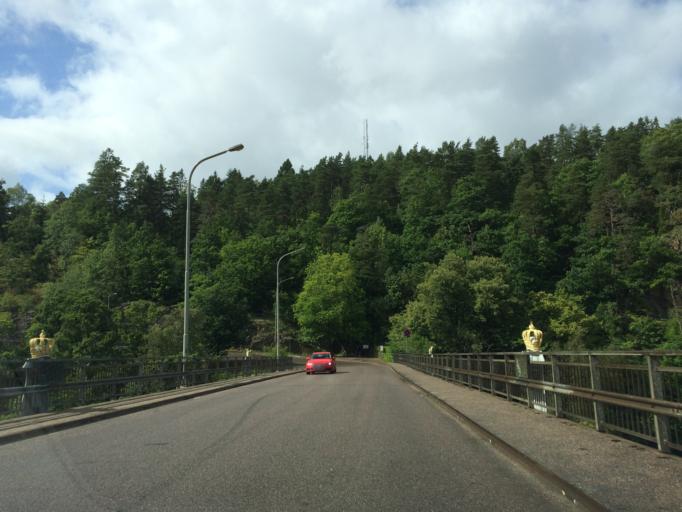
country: SE
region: Vaestra Goetaland
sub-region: Trollhattan
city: Trollhattan
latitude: 58.2802
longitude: 12.2775
